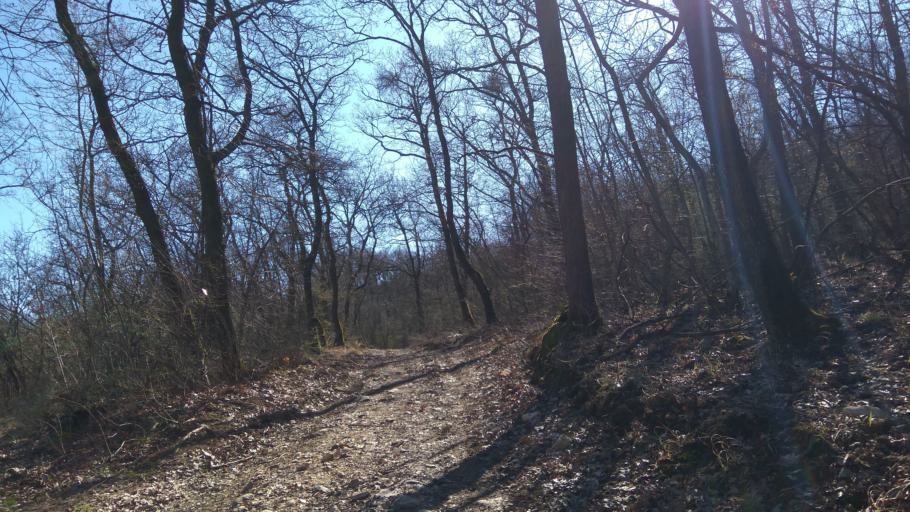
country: HU
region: Pest
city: Csobanka
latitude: 47.6360
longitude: 18.9803
